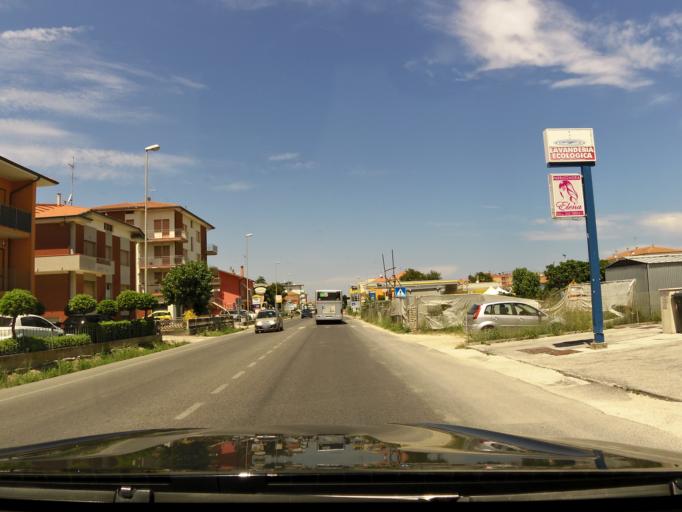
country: IT
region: The Marches
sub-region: Provincia di Pesaro e Urbino
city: Marotta
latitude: 43.7649
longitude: 13.1446
